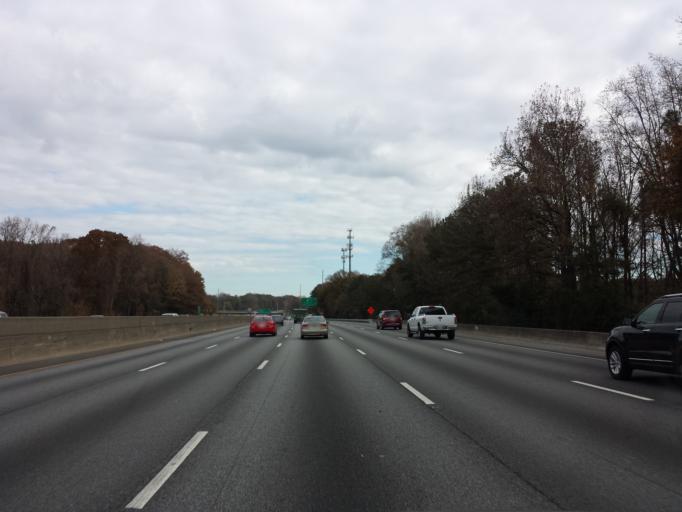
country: US
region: Georgia
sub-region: Fulton County
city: Sandy Springs
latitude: 33.9124
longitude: -84.3867
